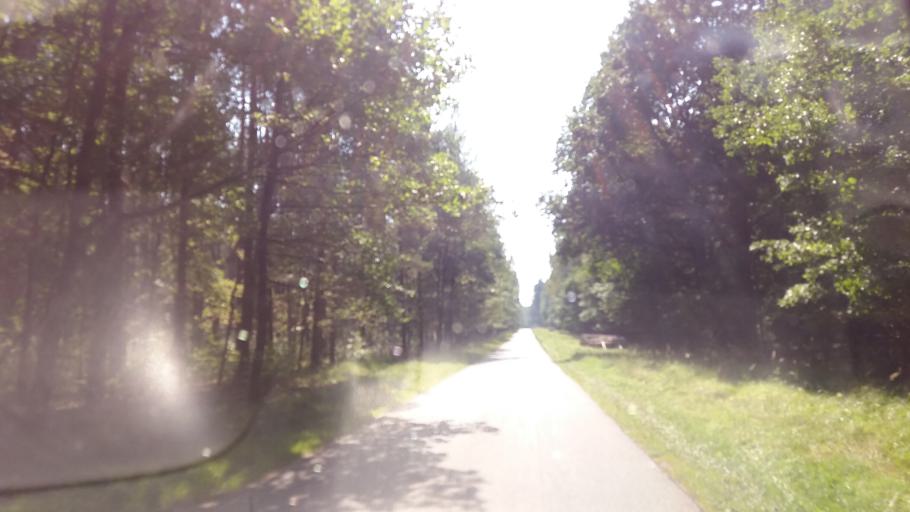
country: PL
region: West Pomeranian Voivodeship
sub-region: Powiat walecki
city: Czlopa
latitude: 53.0891
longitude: 15.9305
